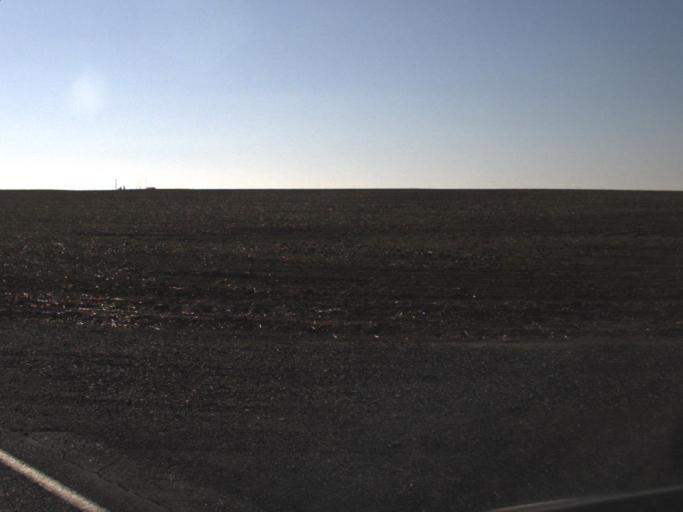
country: US
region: Washington
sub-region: Adams County
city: Ritzville
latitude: 47.0359
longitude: -118.6633
